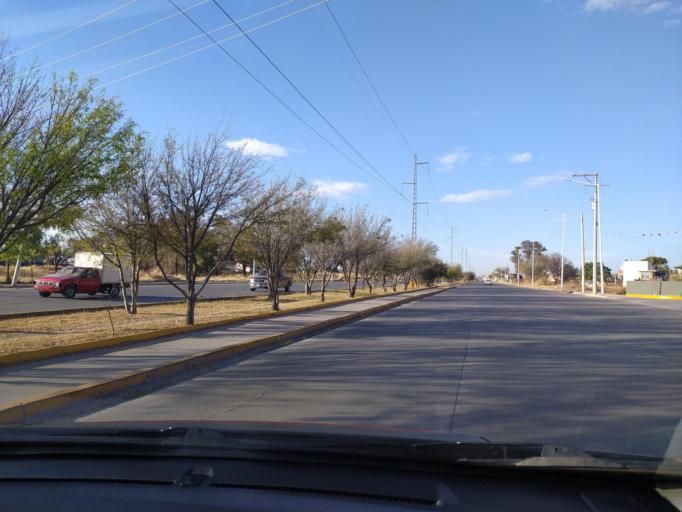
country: MX
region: Guanajuato
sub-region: Purisima del Rincon
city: Monte Grande
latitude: 21.0048
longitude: -101.8701
